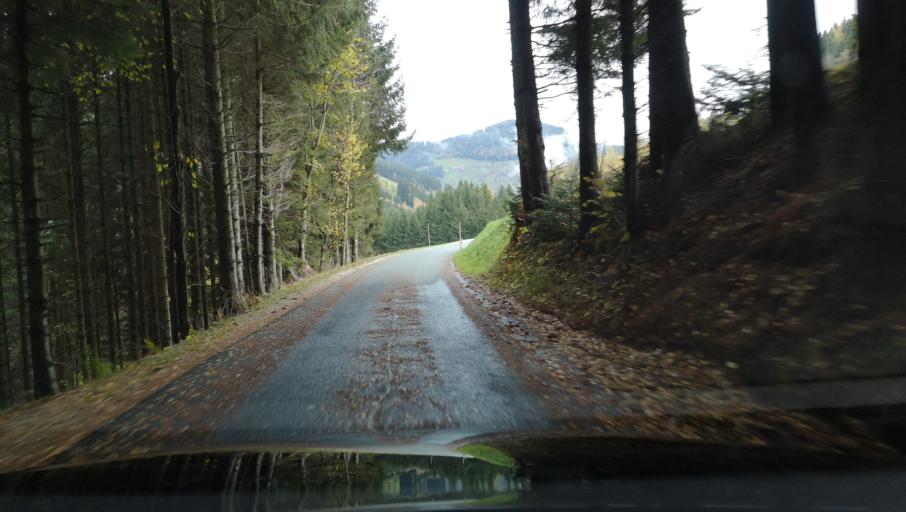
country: AT
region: Styria
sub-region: Politischer Bezirk Weiz
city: Gasen
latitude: 47.3562
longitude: 15.6016
